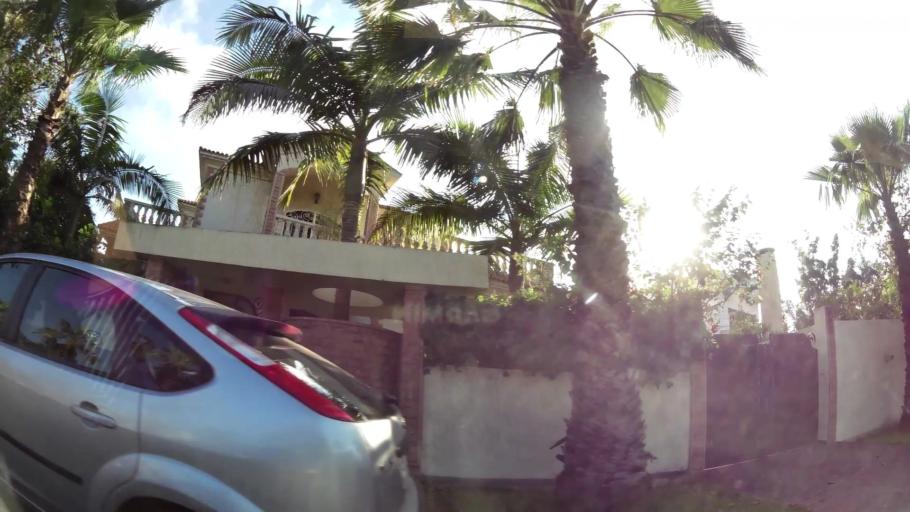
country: MA
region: Rabat-Sale-Zemmour-Zaer
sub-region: Rabat
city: Rabat
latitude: 33.9612
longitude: -6.8525
